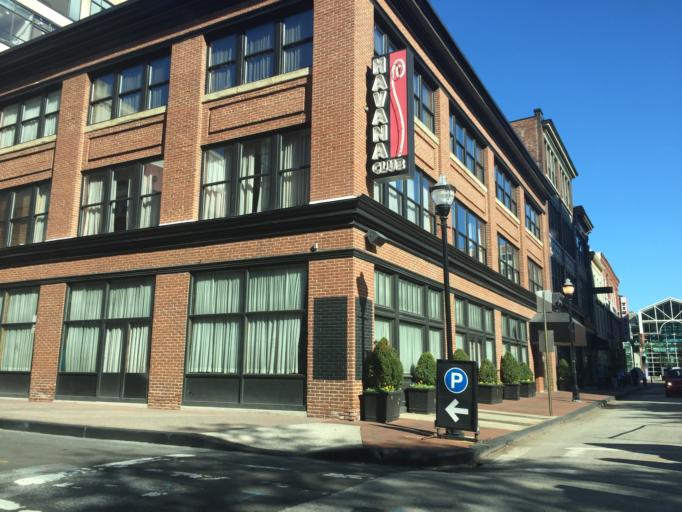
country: US
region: Maryland
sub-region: City of Baltimore
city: Baltimore
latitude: 39.2887
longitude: -76.6081
